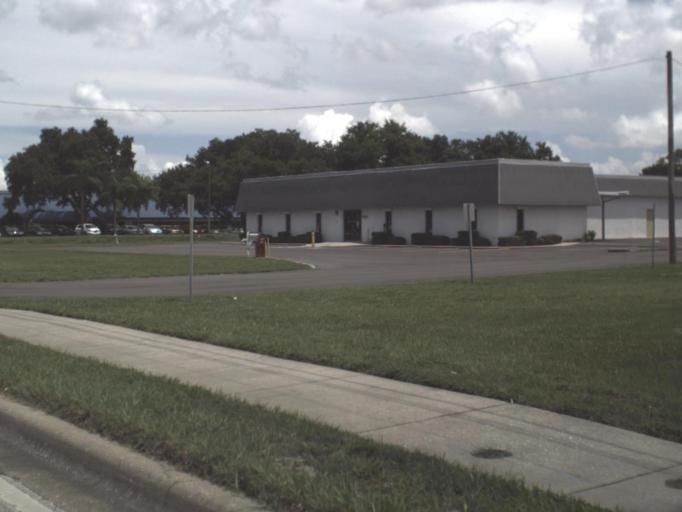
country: US
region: Florida
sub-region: Pinellas County
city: South Highpoint
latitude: 27.9002
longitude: -82.7004
